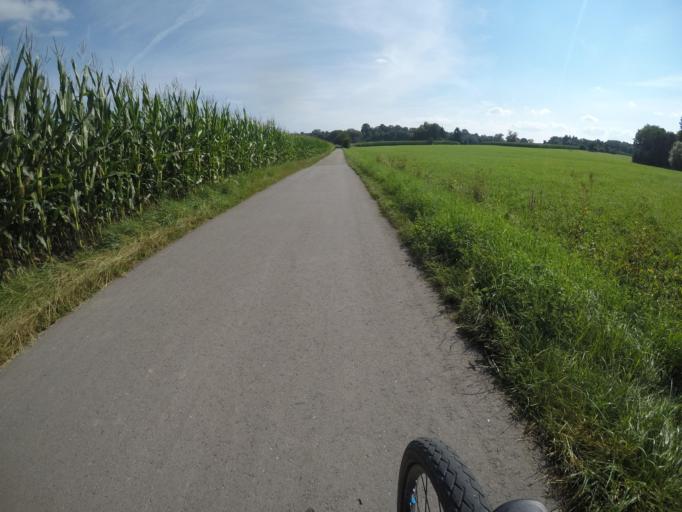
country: DE
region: Baden-Wuerttemberg
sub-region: Karlsruhe Region
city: Olbronn-Durrn
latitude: 48.9635
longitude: 8.7553
